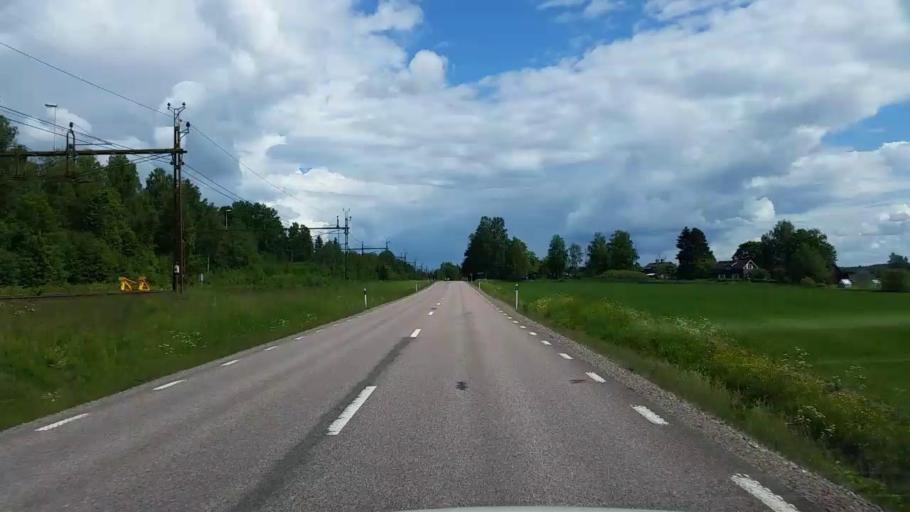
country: SE
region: Dalarna
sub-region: Avesta Kommun
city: Avesta
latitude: 60.1555
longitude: 16.2513
